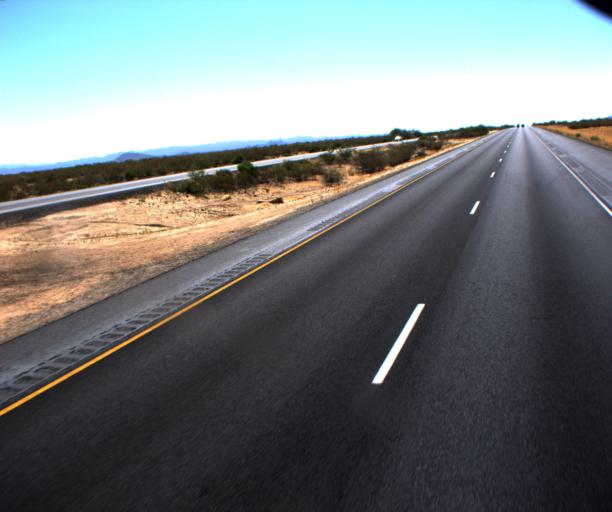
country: US
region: Arizona
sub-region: Yavapai County
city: Congress
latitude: 34.0729
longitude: -112.8786
